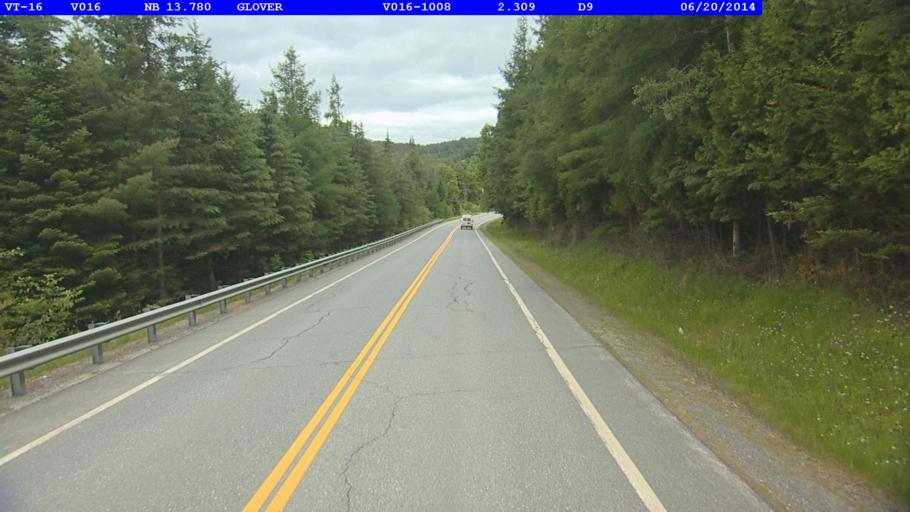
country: US
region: Vermont
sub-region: Caledonia County
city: Hardwick
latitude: 44.6572
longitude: -72.1978
